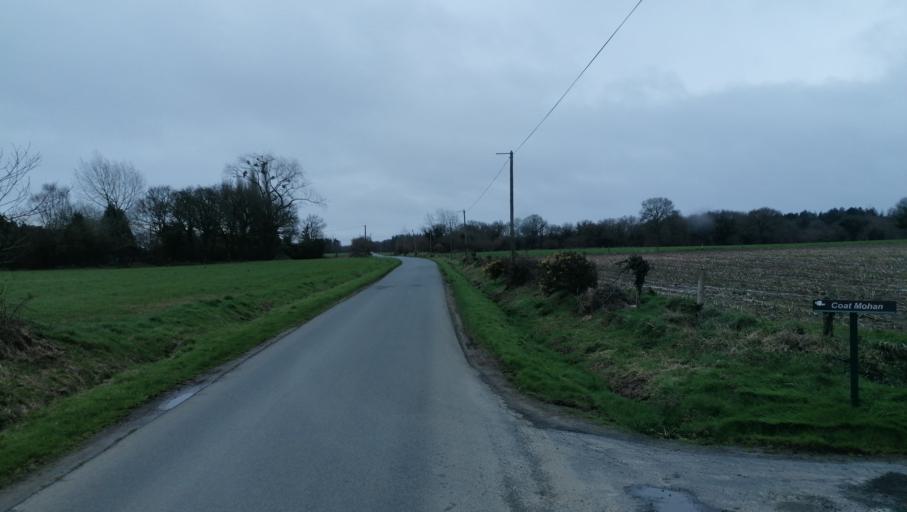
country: FR
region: Brittany
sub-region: Departement des Cotes-d'Armor
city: Saint-Agathon
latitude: 48.5640
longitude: -3.0556
